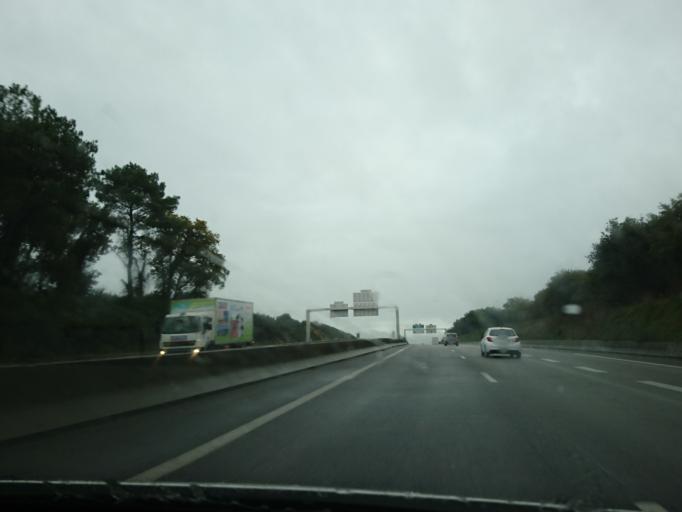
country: FR
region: Brittany
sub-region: Departement du Morbihan
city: Theix
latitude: 47.6433
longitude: -2.6932
